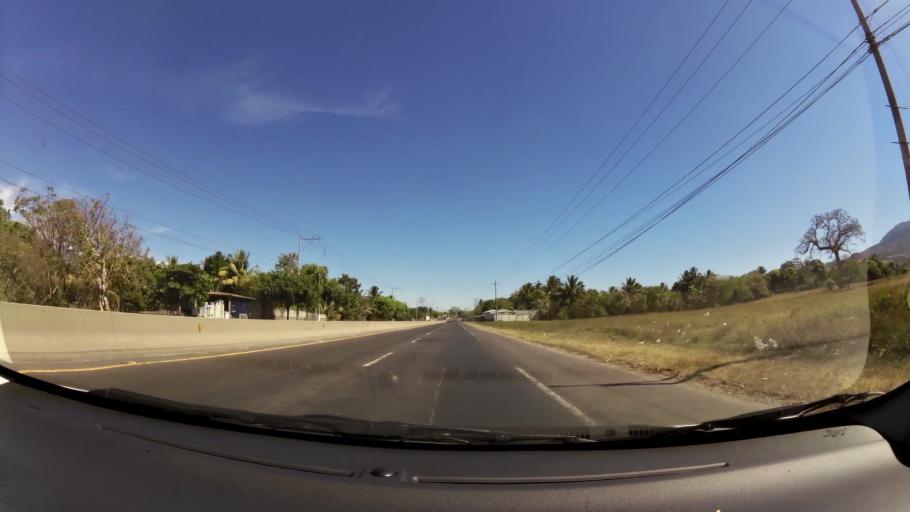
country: SV
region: La Libertad
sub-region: Distrito de Quezaltepeque
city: Quezaltepeque
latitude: 13.7960
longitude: -89.3445
